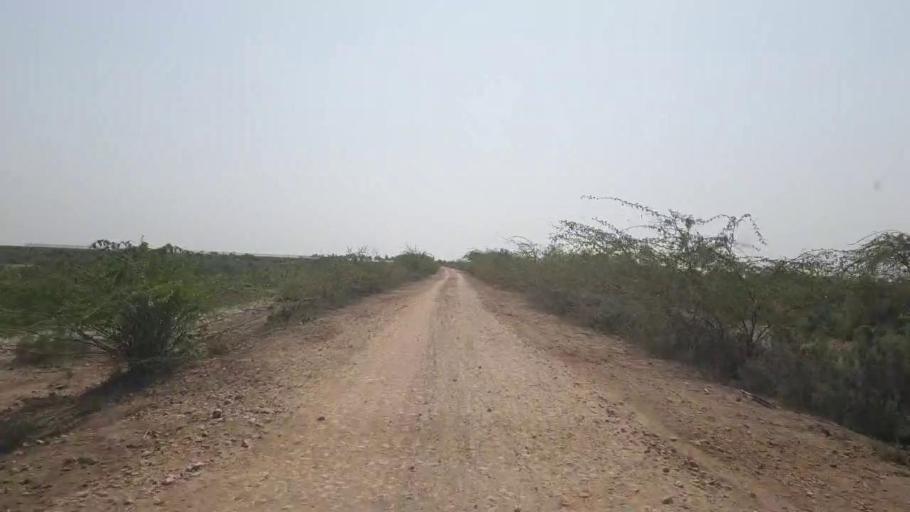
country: PK
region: Sindh
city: Jati
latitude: 24.3853
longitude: 68.5990
